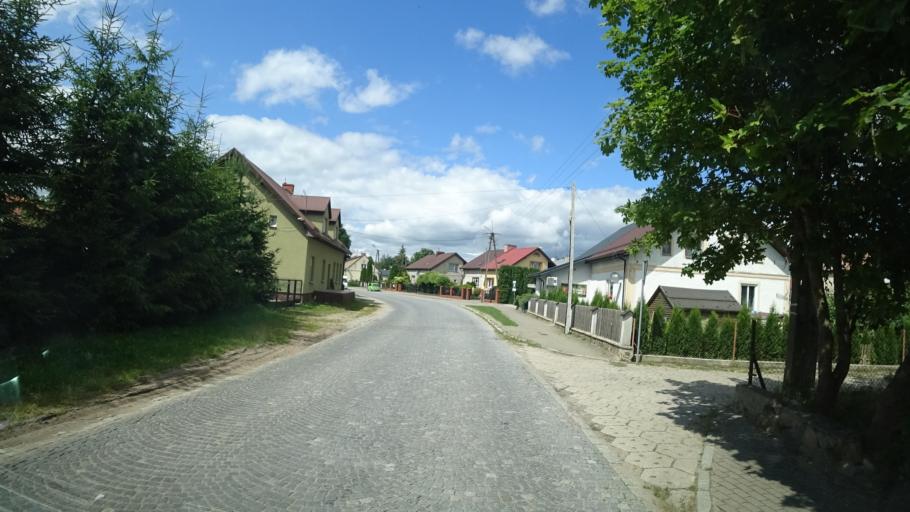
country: PL
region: Warmian-Masurian Voivodeship
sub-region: Powiat goldapski
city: Banie Mazurskie
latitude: 54.2168
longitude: 22.1555
